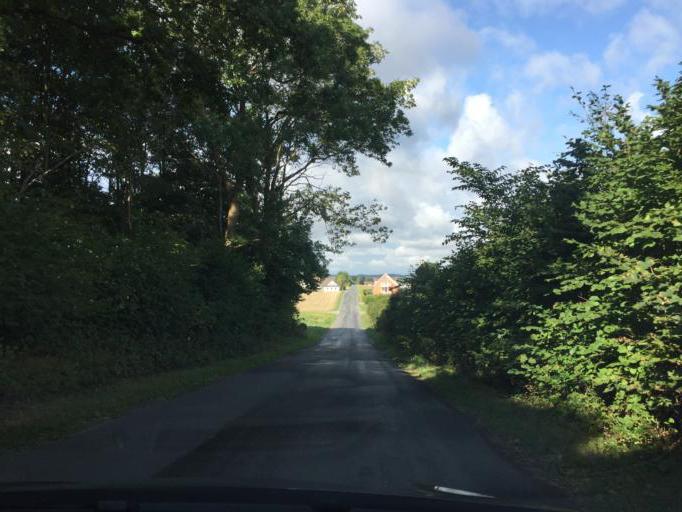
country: DK
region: South Denmark
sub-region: Faaborg-Midtfyn Kommune
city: Faaborg
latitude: 55.1961
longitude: 10.2685
